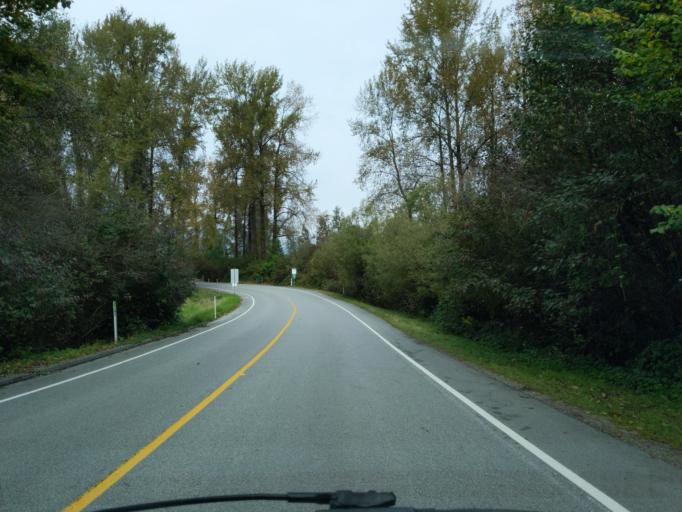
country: CA
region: British Columbia
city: Maple Ridge
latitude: 49.1988
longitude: -122.5941
